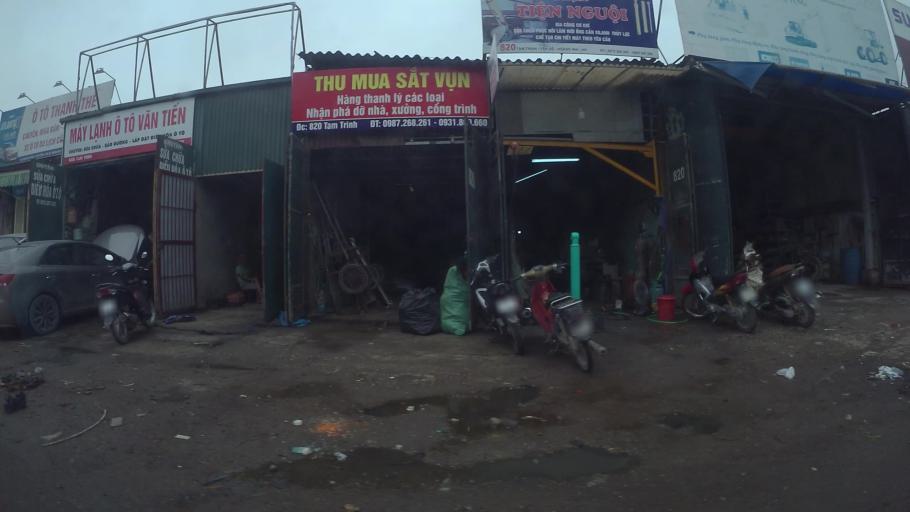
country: VN
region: Ha Noi
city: Van Dien
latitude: 20.9746
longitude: 105.8659
